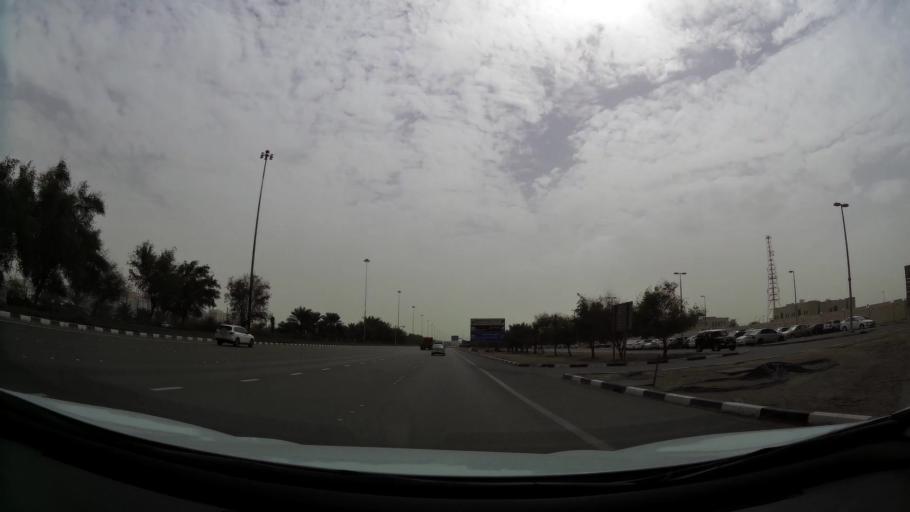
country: AE
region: Abu Dhabi
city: Abu Dhabi
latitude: 24.3409
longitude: 54.5261
